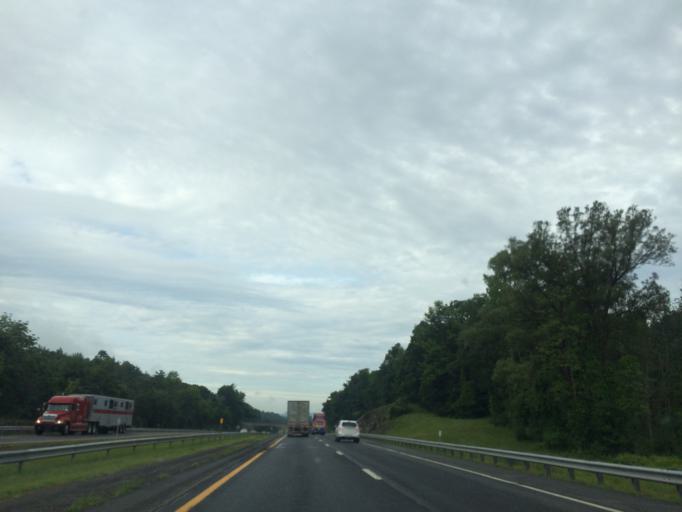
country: US
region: New York
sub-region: Greene County
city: Jefferson Heights
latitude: 42.1864
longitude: -73.9239
